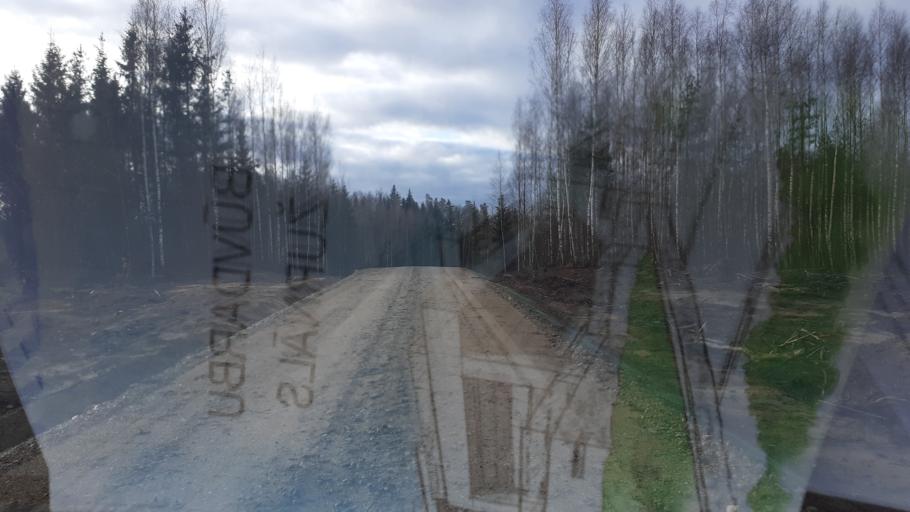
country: LV
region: Skrunda
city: Skrunda
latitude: 56.7905
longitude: 21.8362
